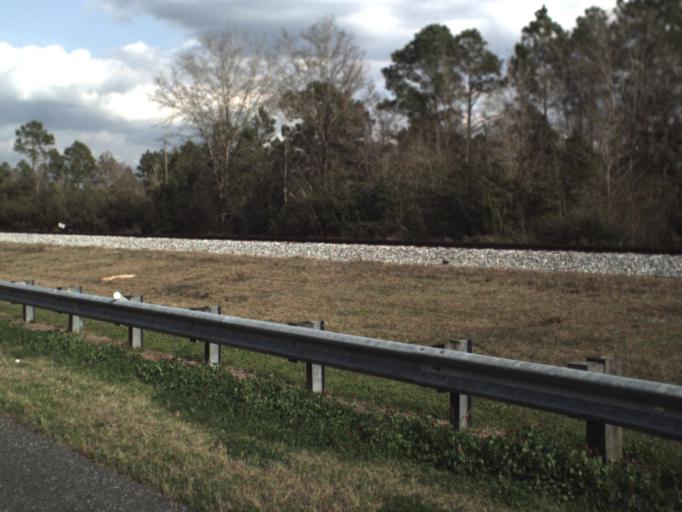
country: US
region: Florida
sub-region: Bay County
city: Youngstown
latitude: 30.3093
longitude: -85.4715
